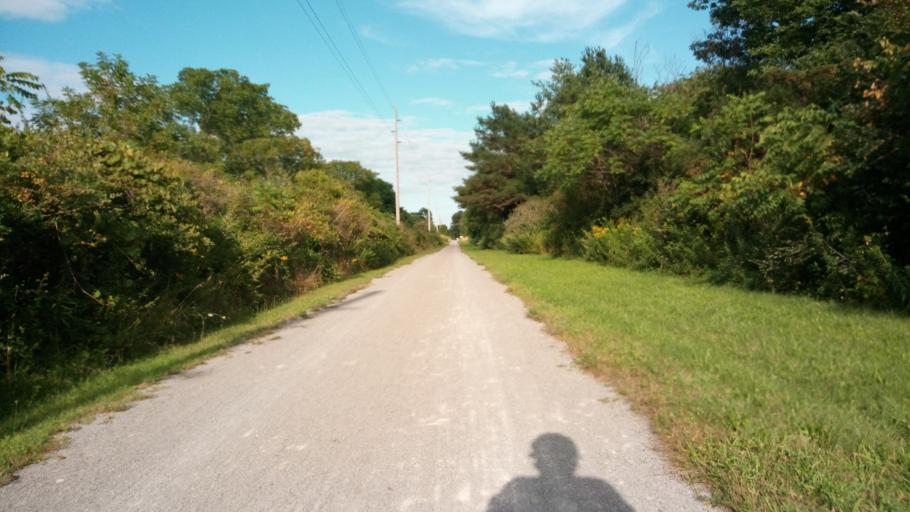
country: US
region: New York
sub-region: Ontario County
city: Victor
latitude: 43.0008
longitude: -77.4972
